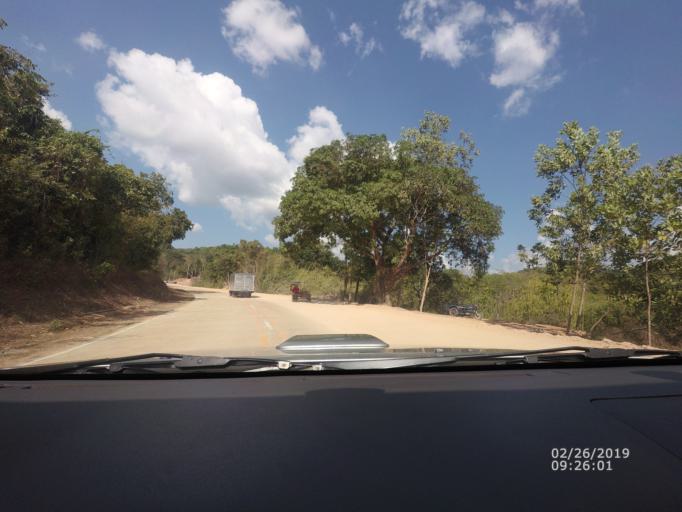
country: PH
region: Mimaropa
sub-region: Province of Palawan
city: Salvacion
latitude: 12.0356
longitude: 120.0372
